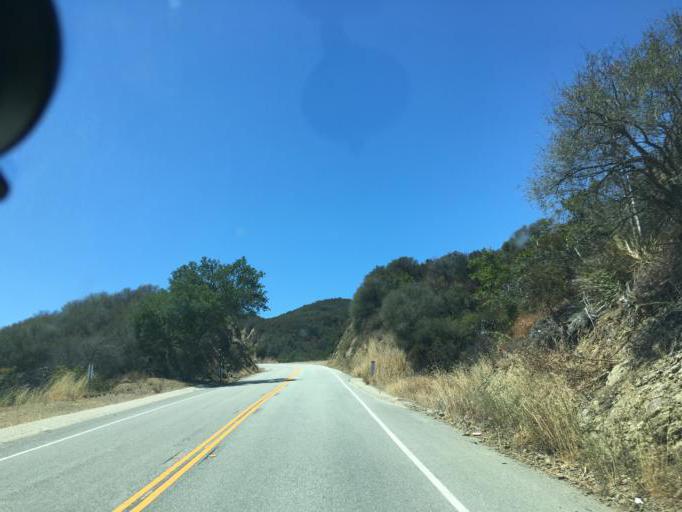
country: US
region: California
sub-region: Los Angeles County
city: Westlake Village
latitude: 34.0824
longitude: -118.8694
